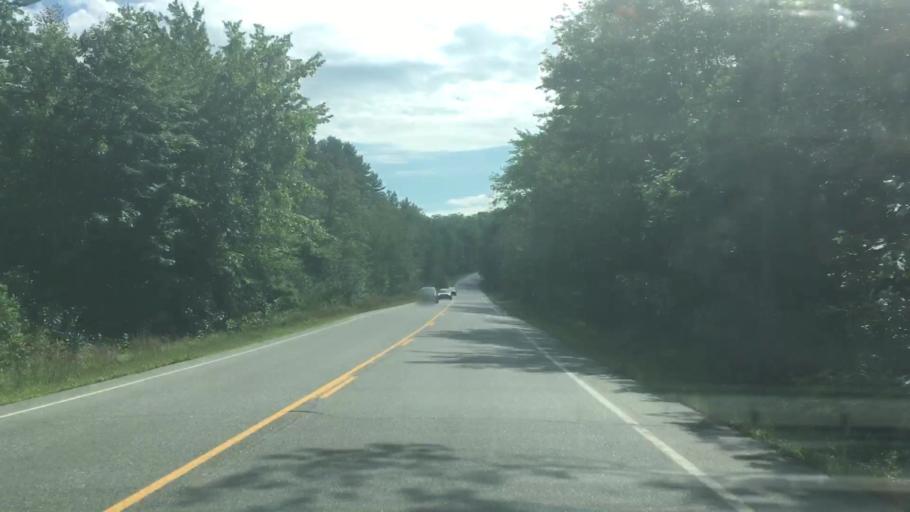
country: US
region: Maine
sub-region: Androscoggin County
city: Poland
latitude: 44.0201
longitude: -70.4411
